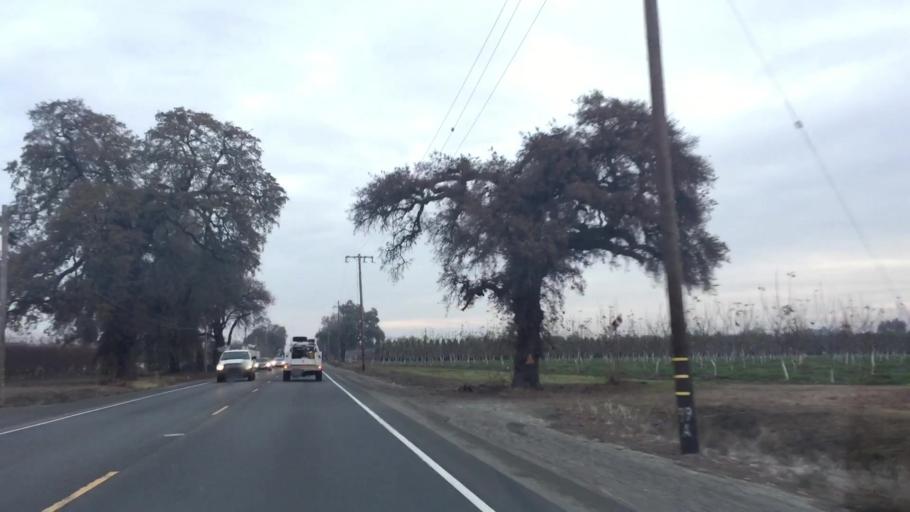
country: US
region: California
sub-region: Sutter County
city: Live Oak
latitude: 39.2264
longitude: -121.6010
